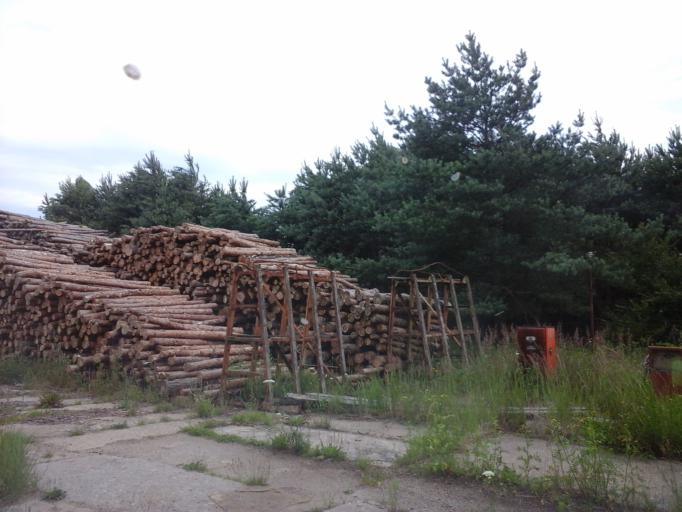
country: PL
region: Lubusz
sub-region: Powiat strzelecko-drezdenecki
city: Dobiegniew
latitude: 53.0901
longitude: 15.7908
